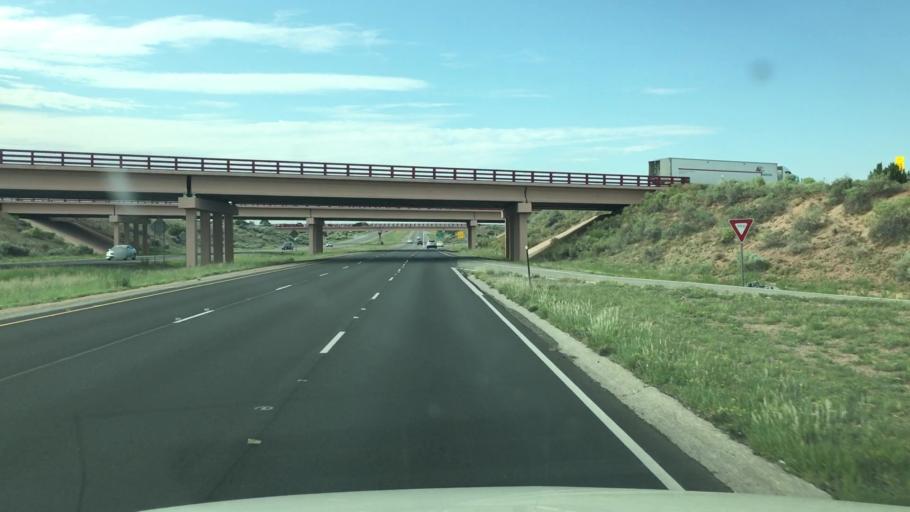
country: US
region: New Mexico
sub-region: Santa Fe County
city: Santa Fe
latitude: 35.6355
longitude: -105.9565
